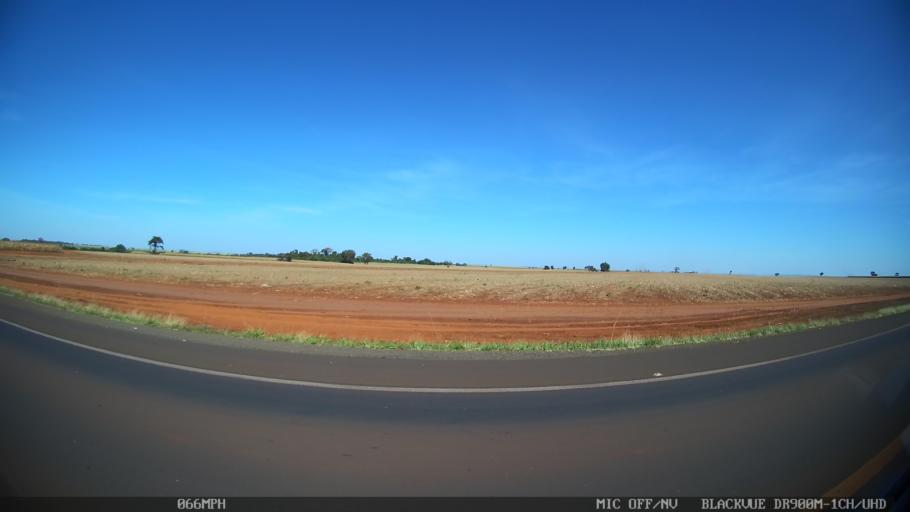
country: BR
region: Sao Paulo
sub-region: Guaira
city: Guaira
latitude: -20.4437
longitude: -48.3405
